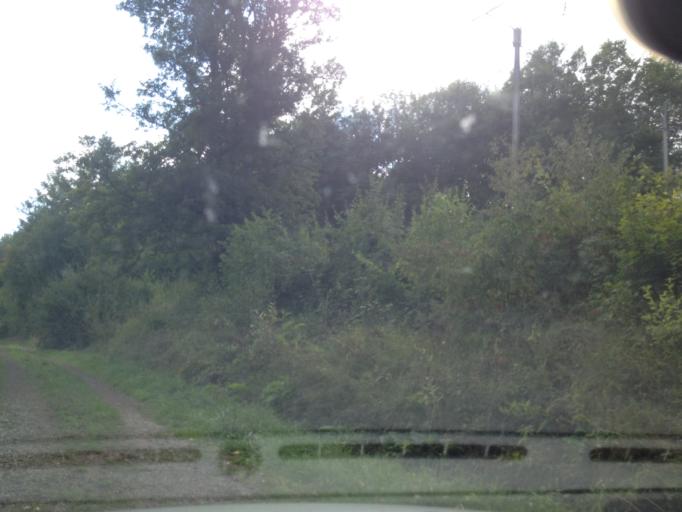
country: FR
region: Franche-Comte
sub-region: Departement de la Haute-Saone
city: Saint-Loup-sur-Semouse
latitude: 47.8327
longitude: 6.2104
